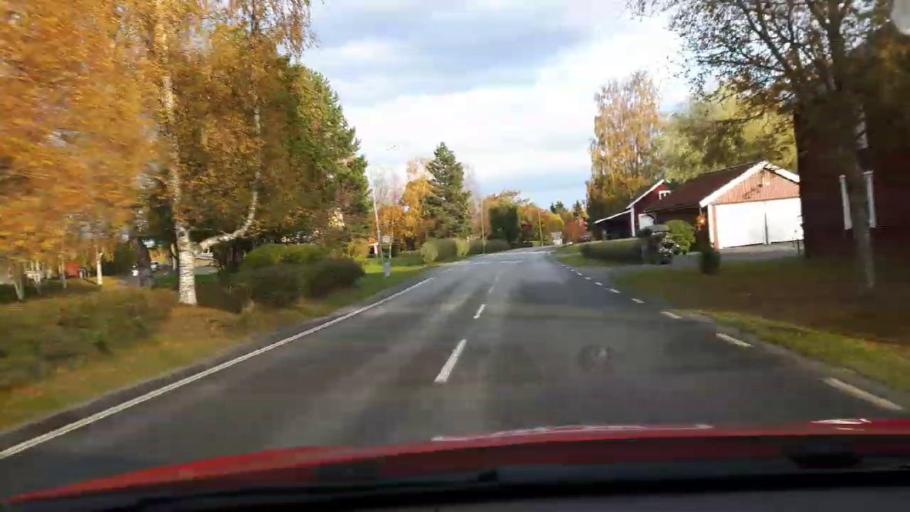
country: SE
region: Jaemtland
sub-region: Krokoms Kommun
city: Krokom
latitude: 63.3447
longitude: 14.5682
